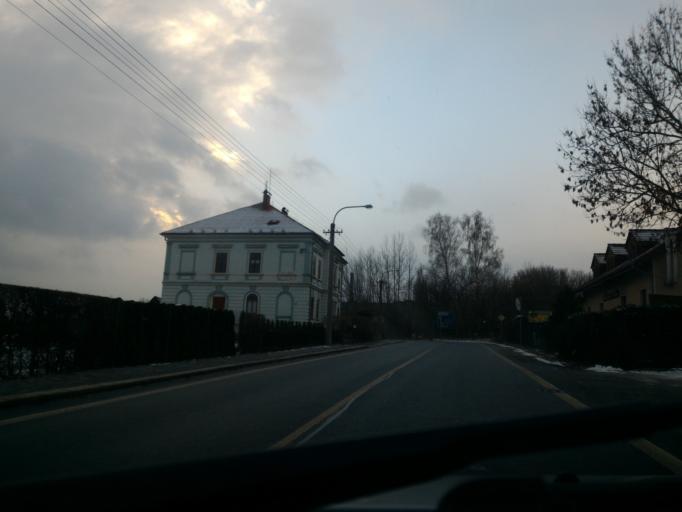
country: CZ
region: Ustecky
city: Varnsdorf
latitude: 50.9163
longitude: 14.6081
